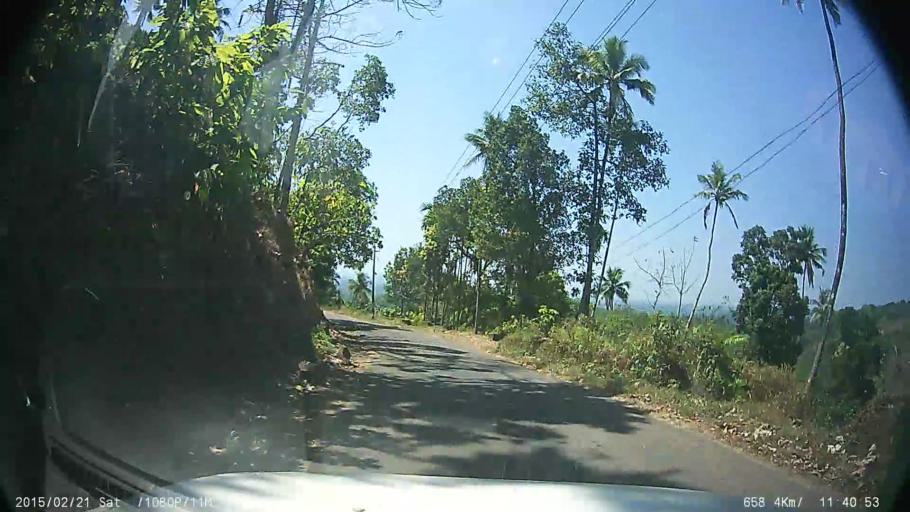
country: IN
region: Kerala
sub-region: Kottayam
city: Lalam
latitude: 9.7978
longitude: 76.7282
